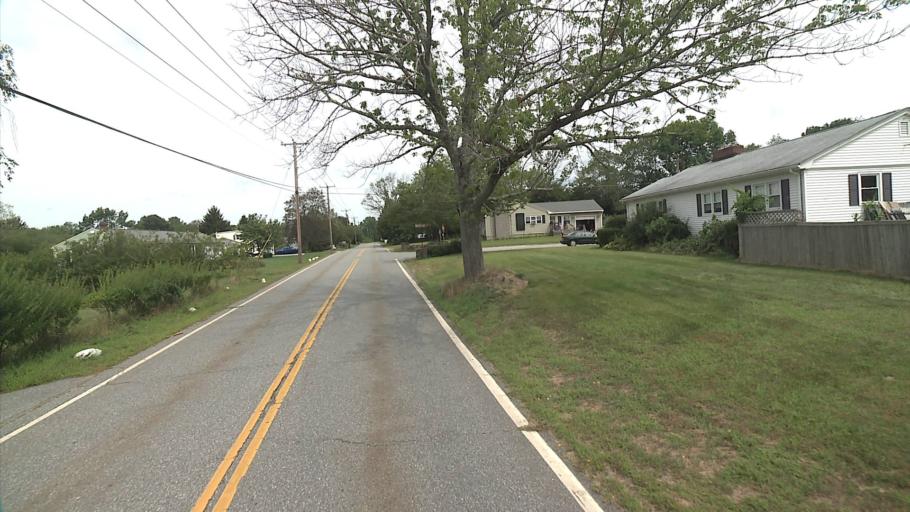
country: US
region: Connecticut
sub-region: Windham County
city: Thompson
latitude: 41.9969
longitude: -71.8449
